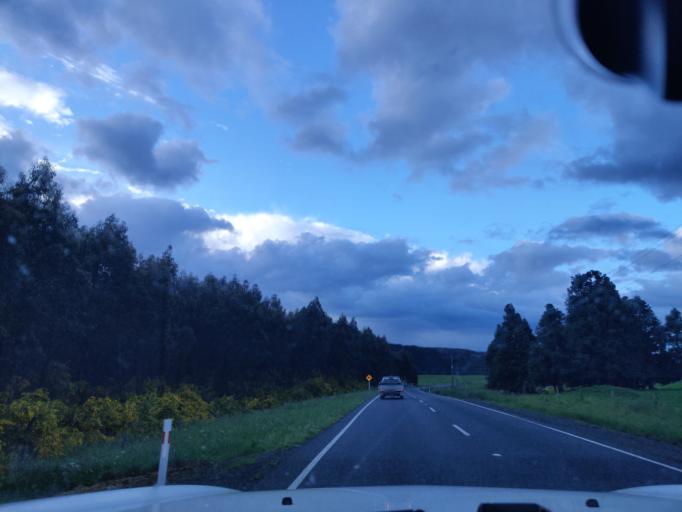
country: NZ
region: Waikato
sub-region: South Waikato District
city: Tokoroa
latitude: -38.3627
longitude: 175.8066
